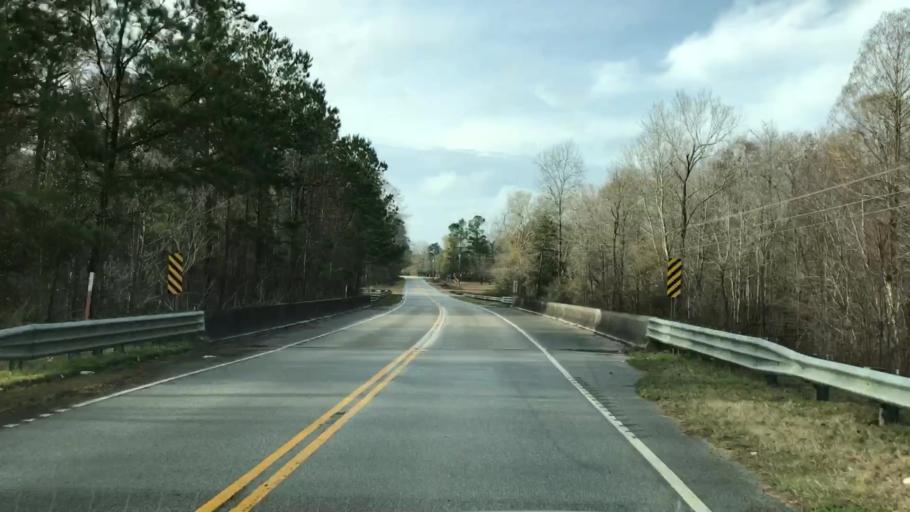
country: US
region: South Carolina
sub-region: Williamsburg County
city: Andrews
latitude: 33.4994
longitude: -79.5136
